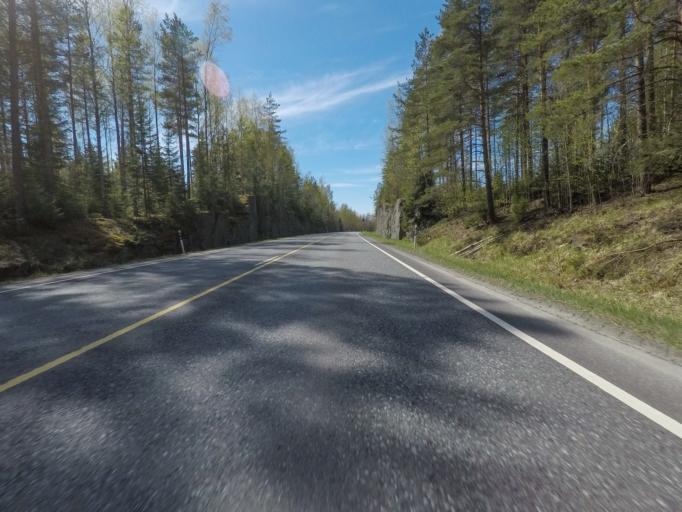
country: FI
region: Haeme
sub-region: Forssa
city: Humppila
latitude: 60.9824
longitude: 23.4415
